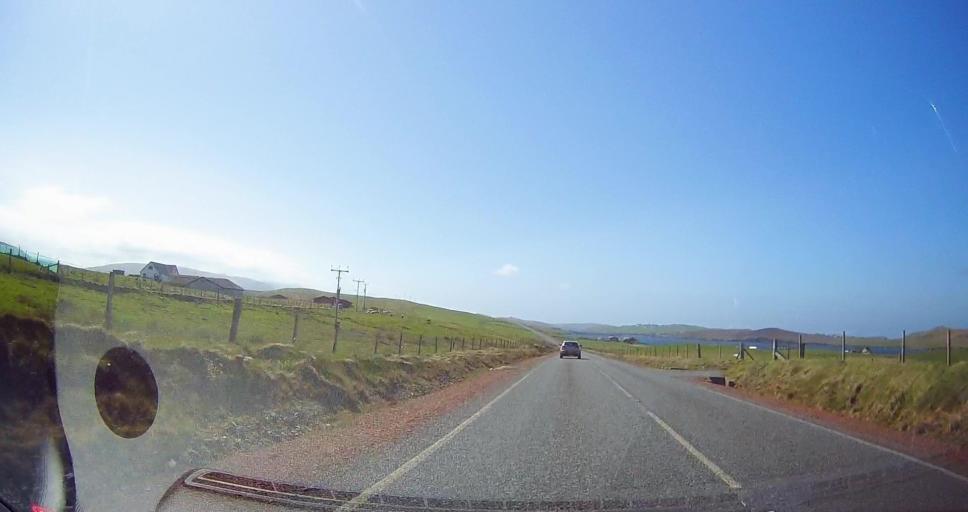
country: GB
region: Scotland
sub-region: Shetland Islands
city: Sandwick
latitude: 60.1210
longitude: -1.2882
